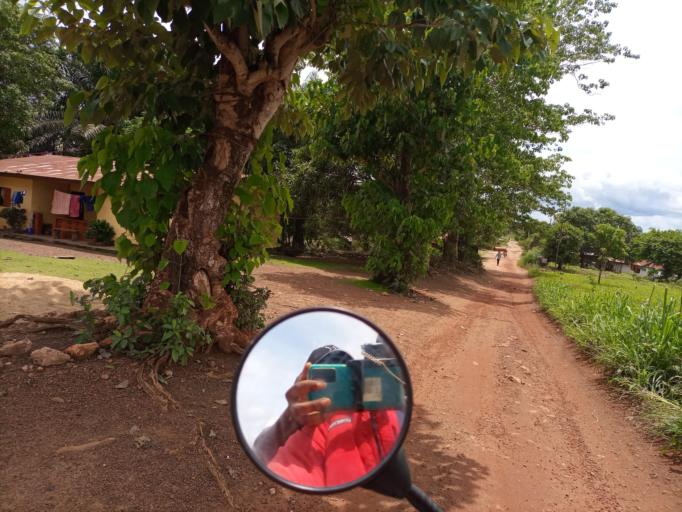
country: SL
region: Southern Province
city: Bo
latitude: 7.9731
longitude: -11.7214
